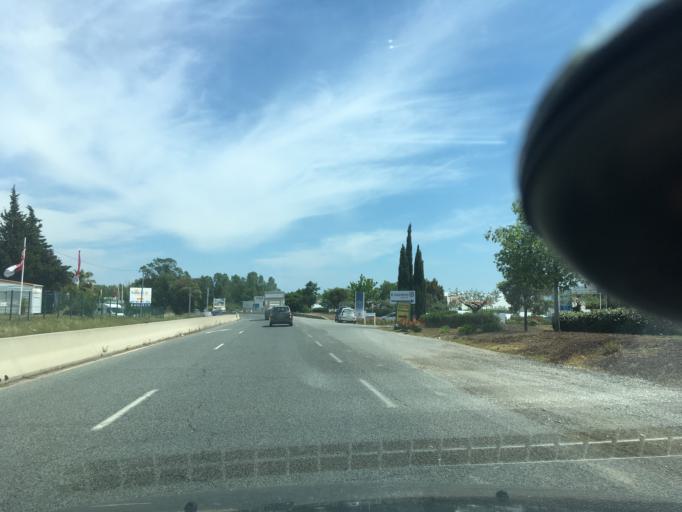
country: FR
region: Provence-Alpes-Cote d'Azur
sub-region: Departement du Var
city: Roquebrune-sur-Argens
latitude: 43.4628
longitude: 6.6434
